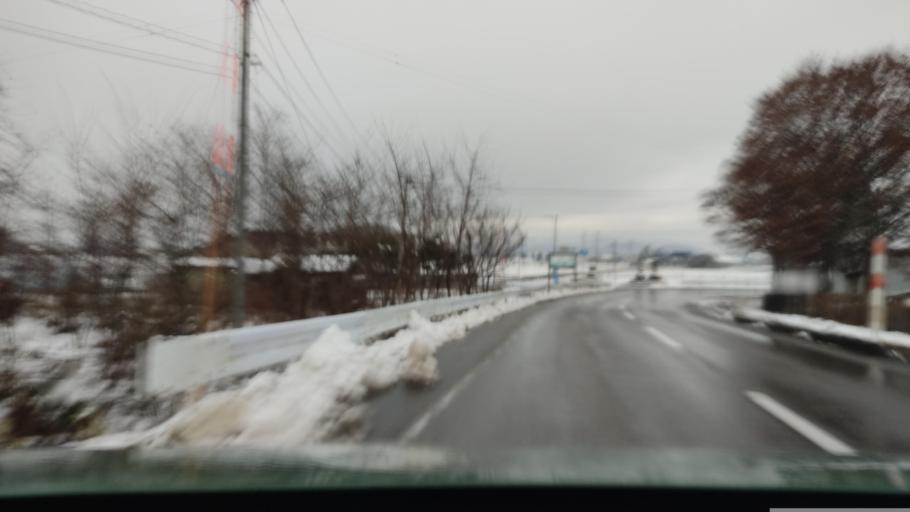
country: JP
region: Akita
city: Omagari
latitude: 39.4575
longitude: 140.5283
